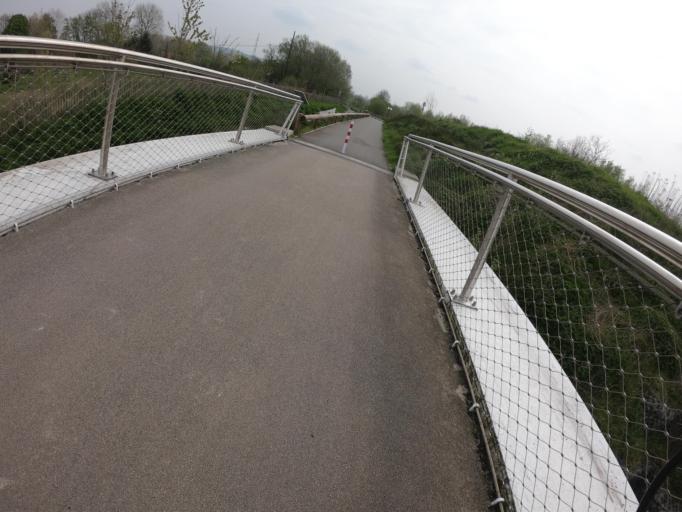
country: BE
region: Flanders
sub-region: Provincie West-Vlaanderen
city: Avelgem
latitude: 50.7611
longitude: 3.4557
